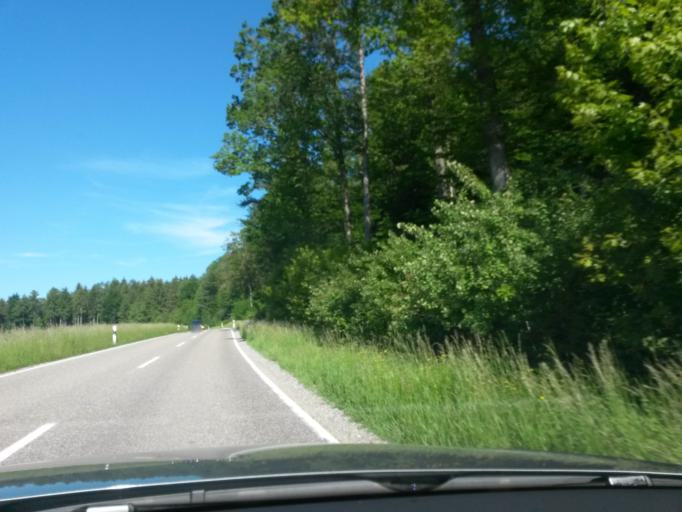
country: DE
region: Baden-Wuerttemberg
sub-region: Tuebingen Region
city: Kanzach
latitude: 48.0815
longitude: 9.5454
